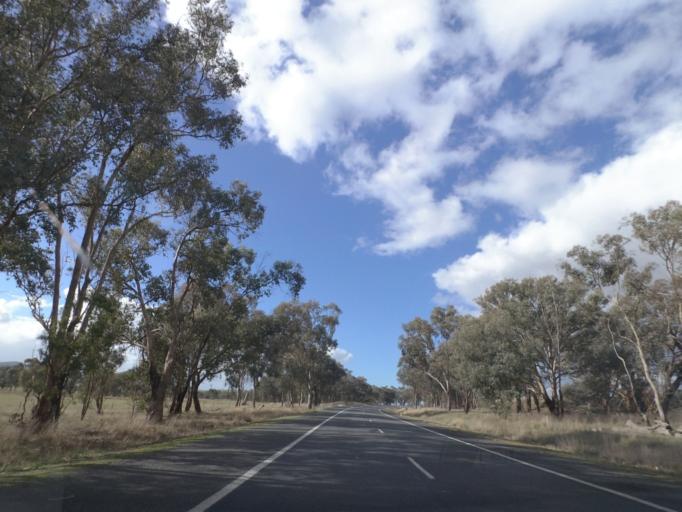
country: AU
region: New South Wales
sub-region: Greater Hume Shire
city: Holbrook
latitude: -35.6749
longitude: 147.3750
